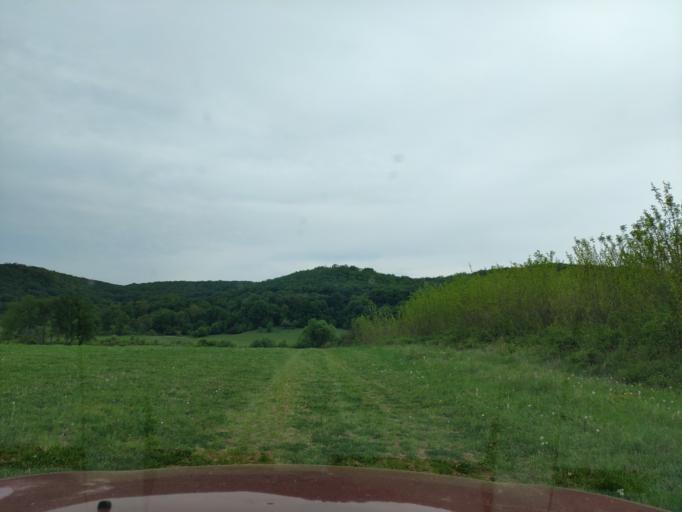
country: SK
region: Banskobystricky
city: Revuca
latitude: 48.5194
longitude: 20.1311
